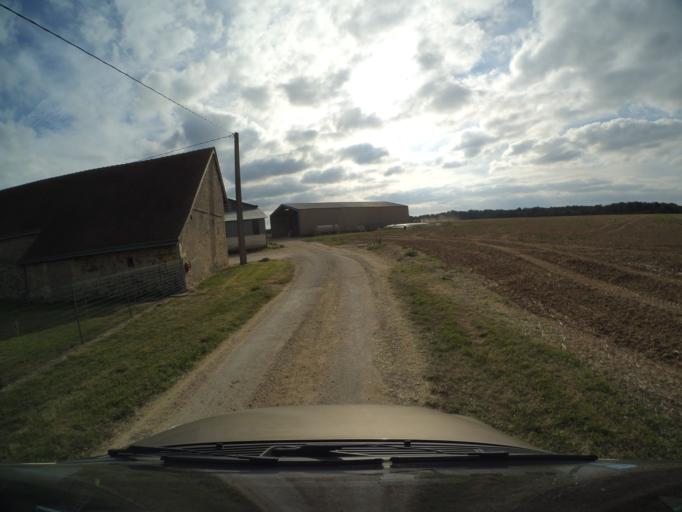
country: FR
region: Centre
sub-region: Departement d'Indre-et-Loire
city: Poce-sur-Cisse
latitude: 47.4663
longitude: 0.9660
